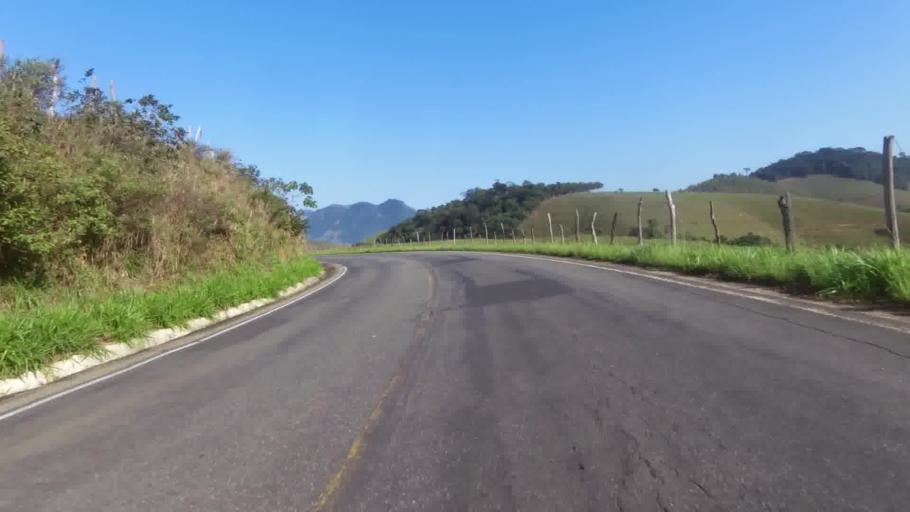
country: BR
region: Espirito Santo
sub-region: Alfredo Chaves
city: Alfredo Chaves
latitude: -20.6610
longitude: -40.7106
